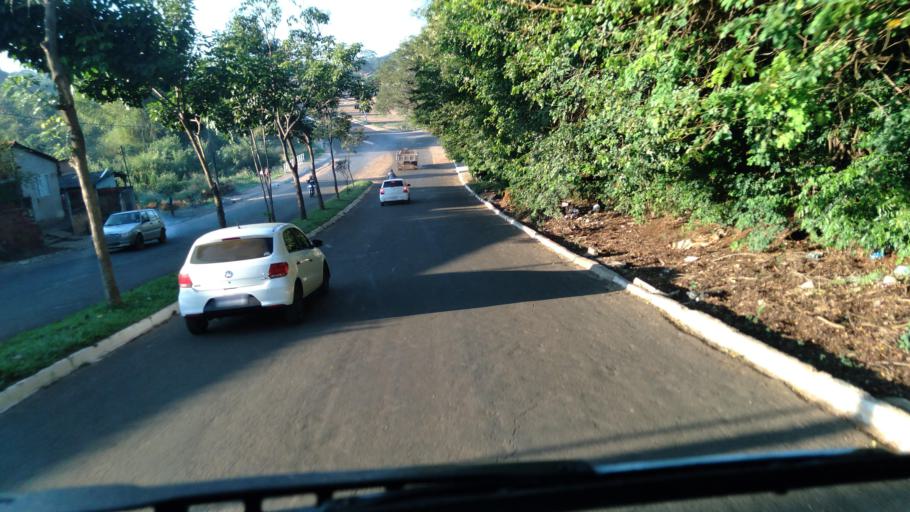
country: BR
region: Goias
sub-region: Mineiros
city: Mineiros
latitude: -17.5774
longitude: -52.5661
